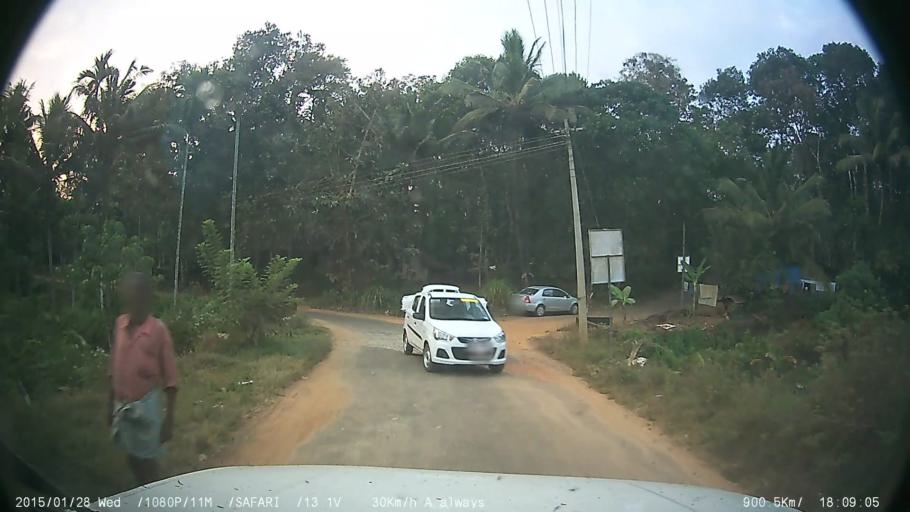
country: IN
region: Kerala
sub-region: Kottayam
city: Palackattumala
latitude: 9.7447
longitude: 76.5760
